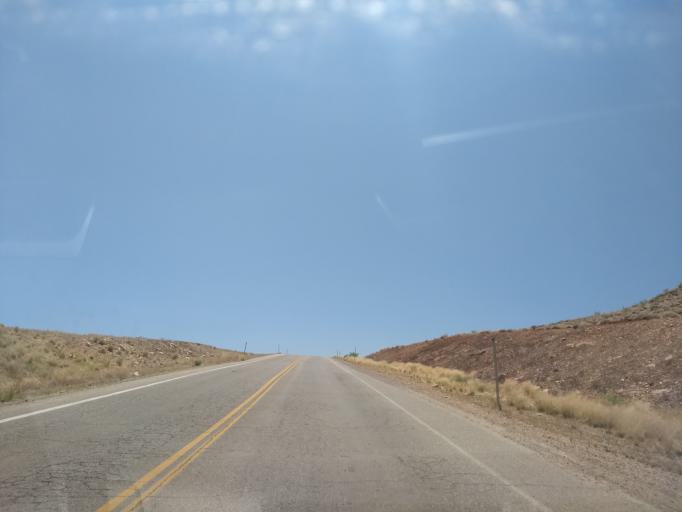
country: US
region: Utah
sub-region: Washington County
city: Washington
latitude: 37.1359
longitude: -113.4589
